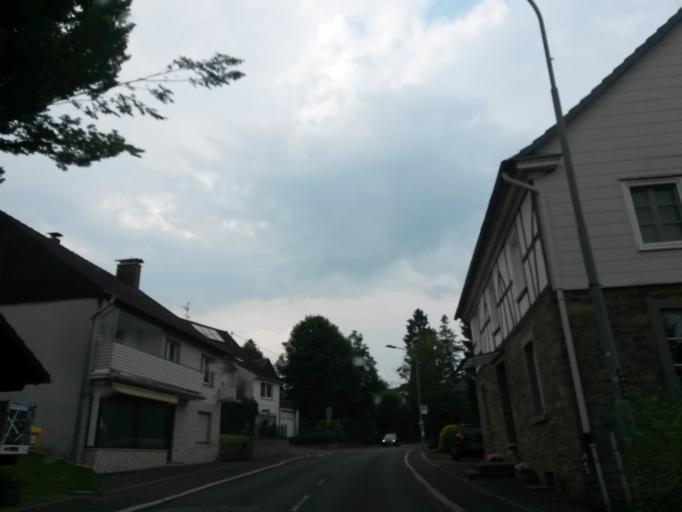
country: DE
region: North Rhine-Westphalia
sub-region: Regierungsbezirk Koln
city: Engelskirchen
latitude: 51.0148
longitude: 7.4683
